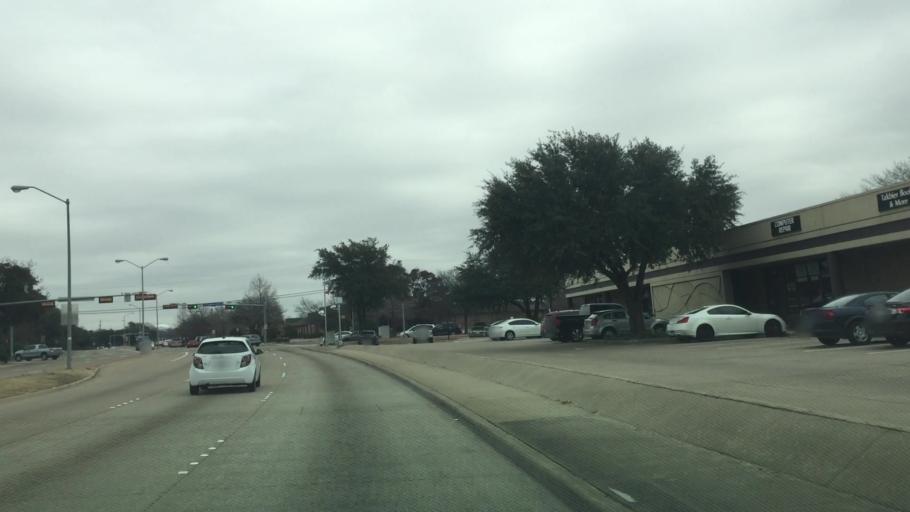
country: US
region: Texas
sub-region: Dallas County
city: Richardson
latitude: 32.9390
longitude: -96.7349
